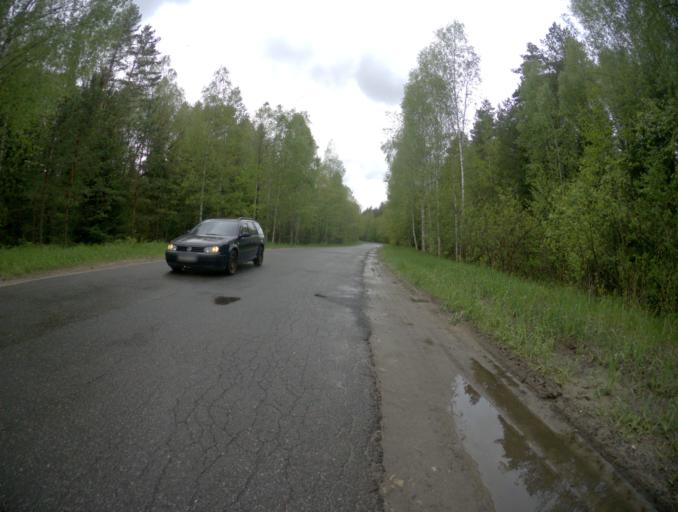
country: RU
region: Vladimir
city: Zolotkovo
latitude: 55.3450
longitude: 40.9867
